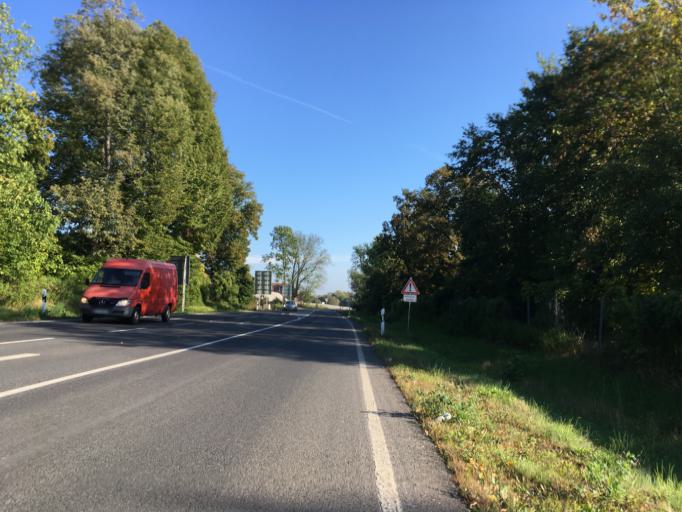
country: PL
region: Lubusz
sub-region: Powiat gorzowski
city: Kostrzyn nad Odra
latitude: 52.5768
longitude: 14.6241
